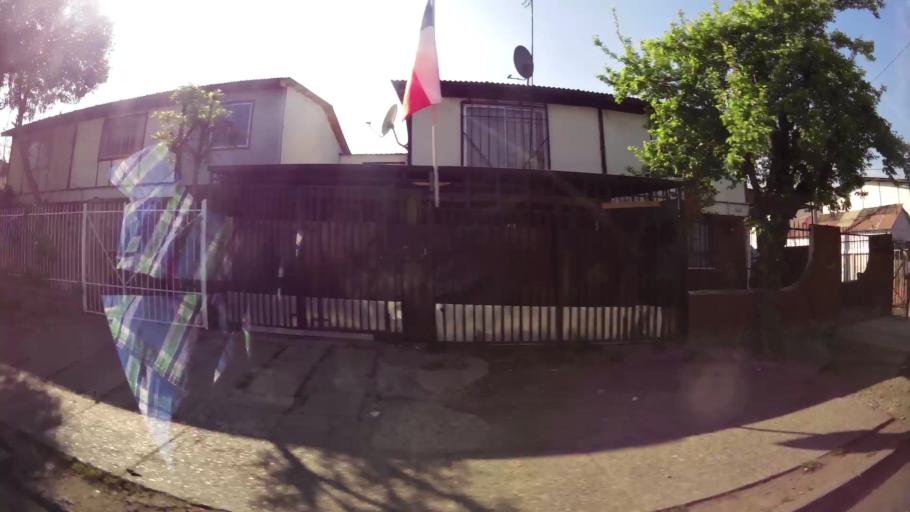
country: CL
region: Santiago Metropolitan
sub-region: Provincia de Santiago
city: Lo Prado
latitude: -33.4585
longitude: -70.7559
